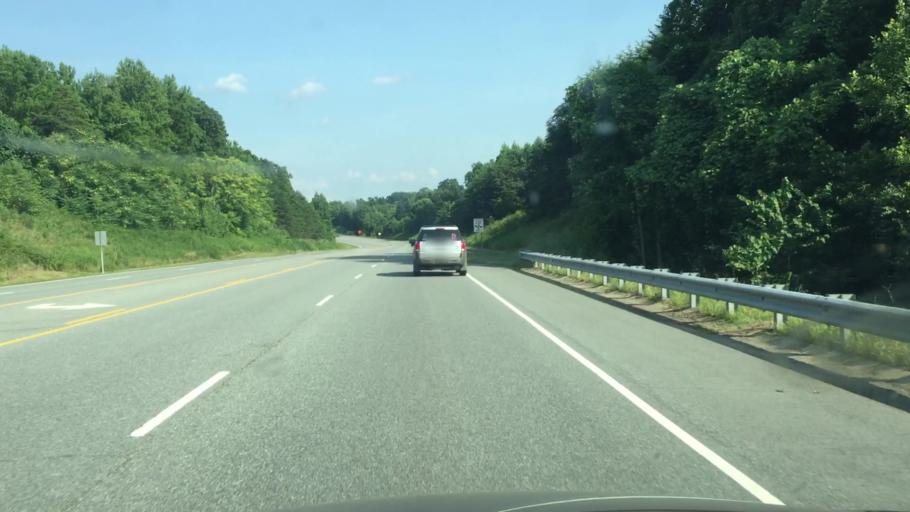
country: US
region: North Carolina
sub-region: Rockingham County
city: Reidsville
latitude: 36.3666
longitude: -79.6426
